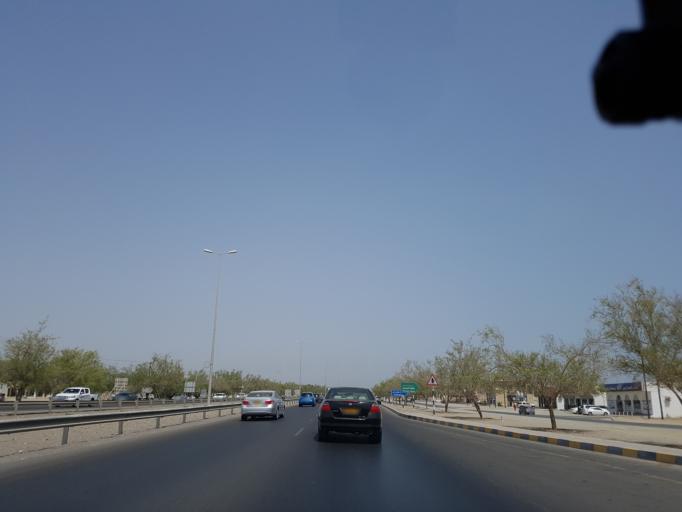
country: OM
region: Al Batinah
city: Saham
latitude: 24.1450
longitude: 56.8735
